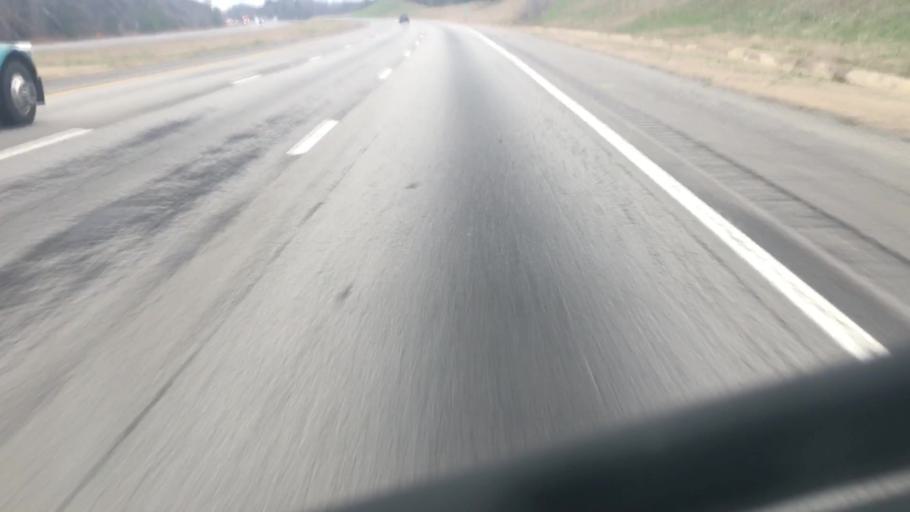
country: US
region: Alabama
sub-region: Walker County
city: Dora
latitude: 33.7096
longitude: -87.1449
